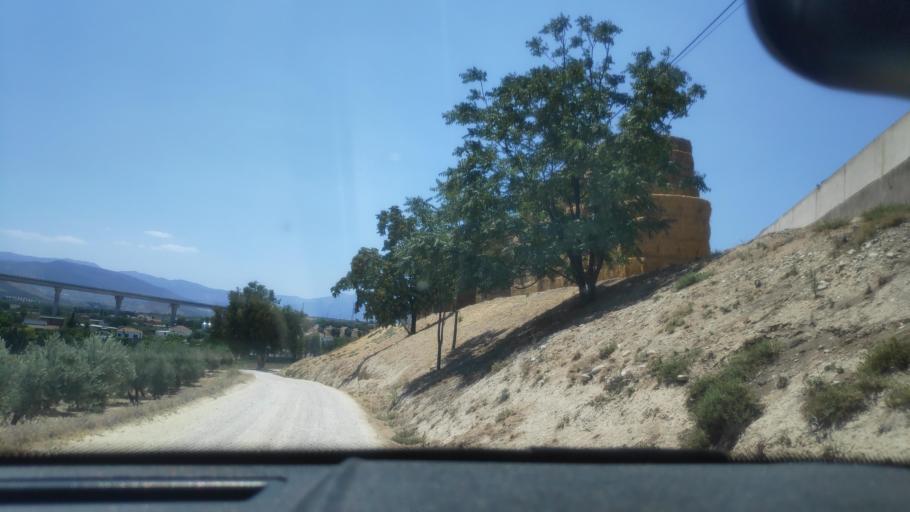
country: ES
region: Andalusia
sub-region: Provincia de Jaen
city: Jaen
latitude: 37.8252
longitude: -3.7592
